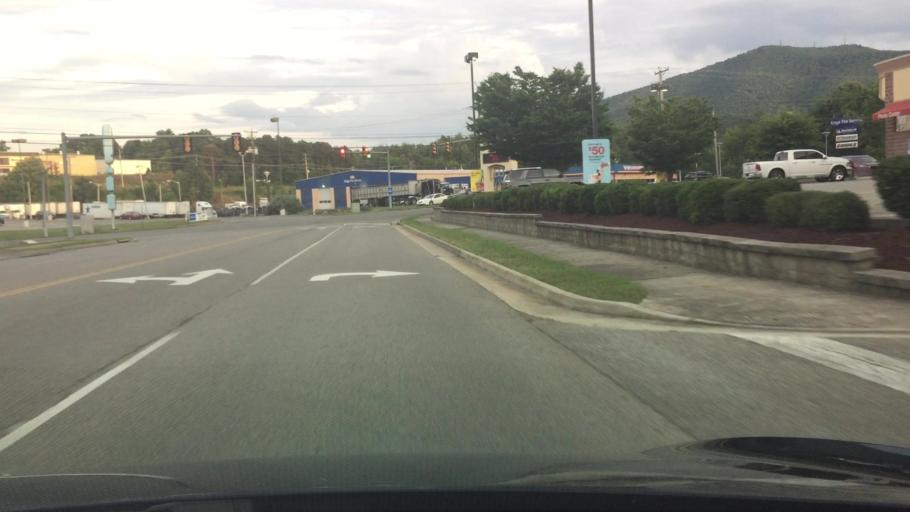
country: US
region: Virginia
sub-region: Pulaski County
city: Pulaski
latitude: 37.0530
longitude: -80.7516
